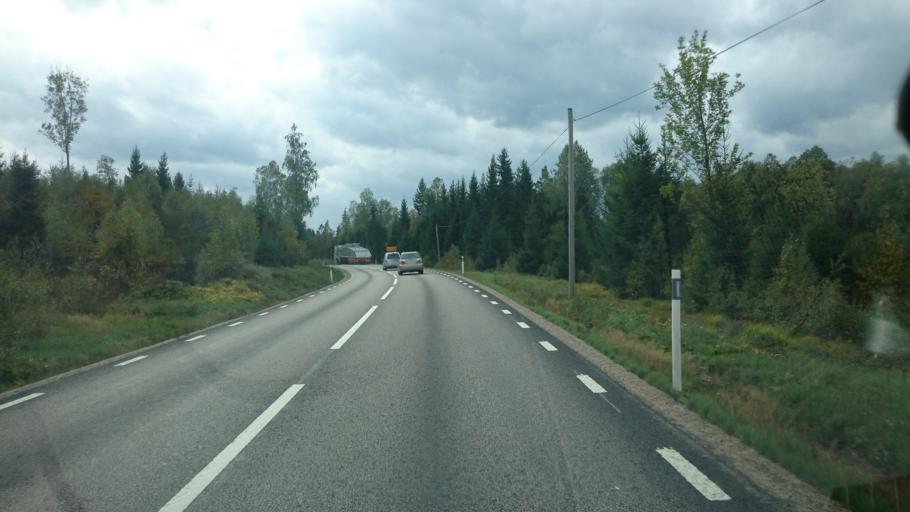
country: SE
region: Vaestra Goetaland
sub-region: Tranemo Kommun
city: Langhem
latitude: 57.6010
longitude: 13.1296
